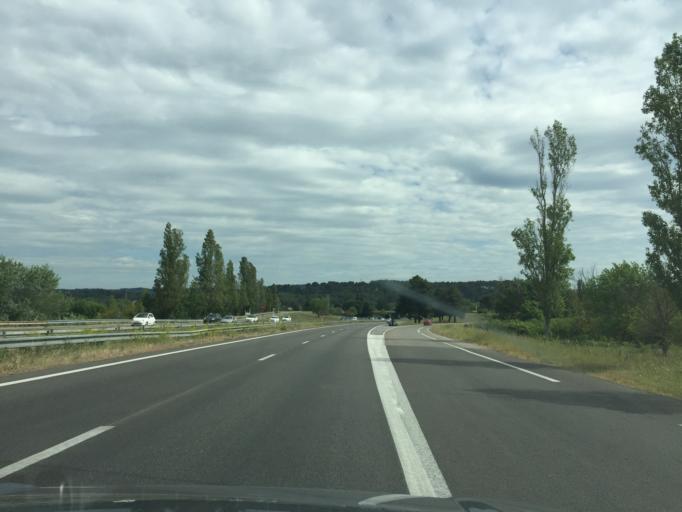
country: FR
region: Provence-Alpes-Cote d'Azur
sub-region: Departement des Bouches-du-Rhone
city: Aix-en-Provence
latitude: 43.5025
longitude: 5.4079
